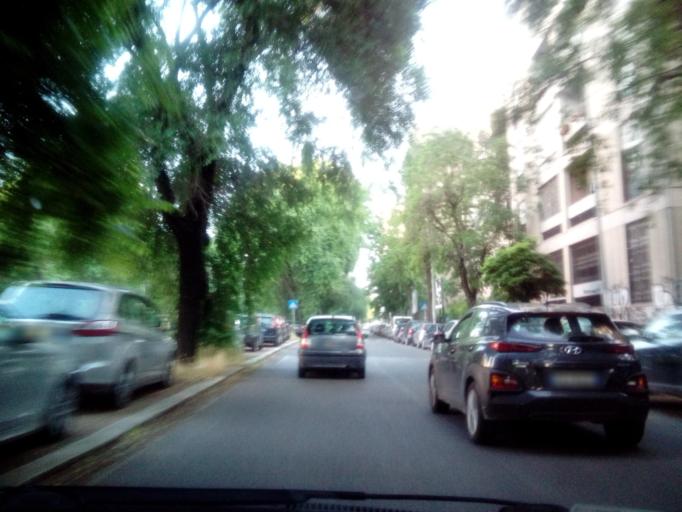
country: IT
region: Latium
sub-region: Citta metropolitana di Roma Capitale
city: Rome
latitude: 41.8587
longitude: 12.5705
